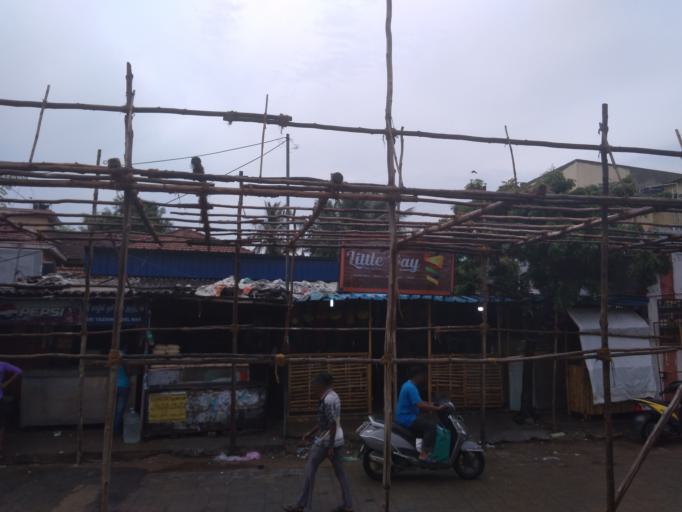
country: IN
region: Tamil Nadu
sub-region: Kancheepuram
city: Perungudi
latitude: 12.9665
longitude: 80.2476
